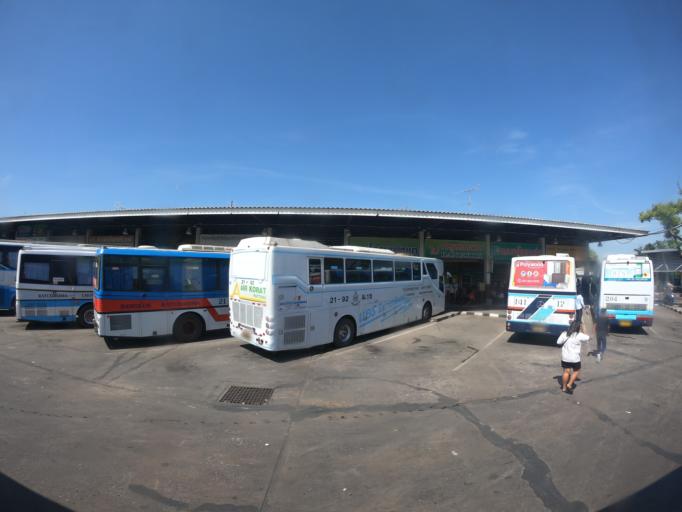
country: TH
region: Nakhon Ratchasima
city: Nakhon Ratchasima
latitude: 14.9895
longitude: 102.0942
